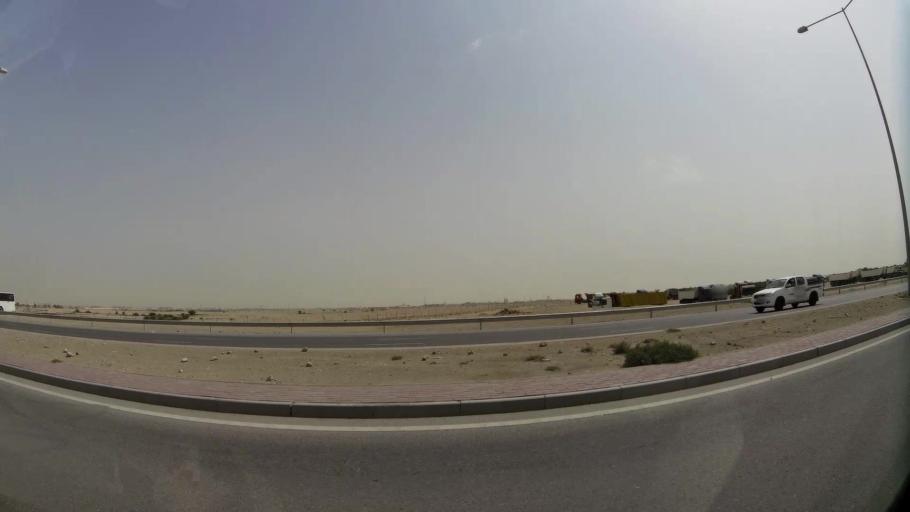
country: QA
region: Baladiyat ar Rayyan
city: Ar Rayyan
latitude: 25.2295
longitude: 51.3875
